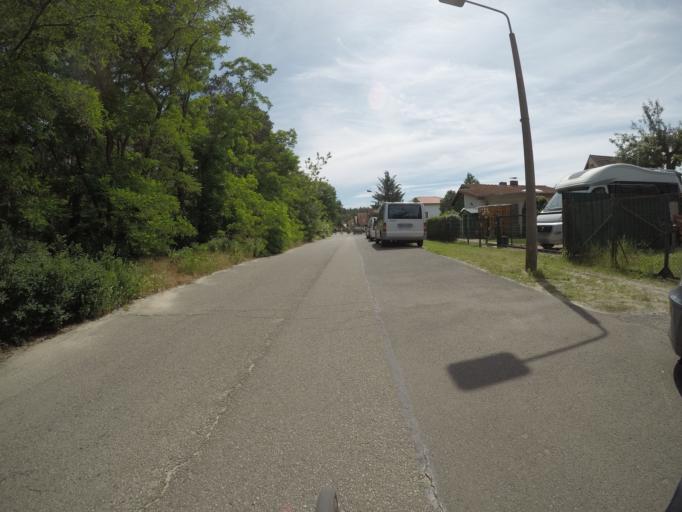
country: DE
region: Berlin
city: Berlin Koepenick
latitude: 52.4668
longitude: 13.5938
